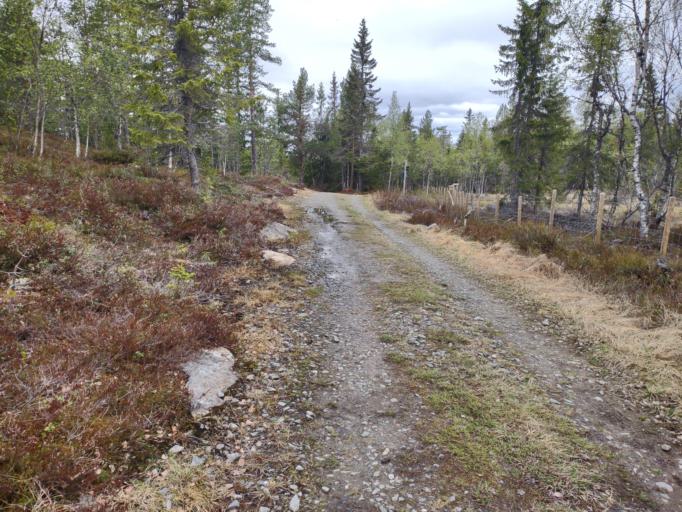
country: NO
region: Oppland
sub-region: Gran
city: Jaren
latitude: 60.4474
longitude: 10.6488
